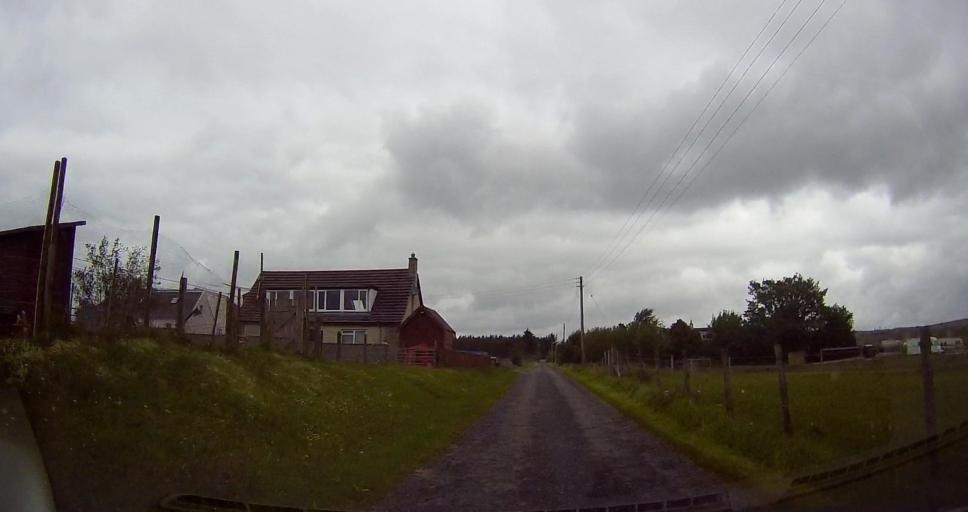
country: GB
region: Scotland
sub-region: Highland
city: Alness
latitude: 58.0630
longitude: -4.4279
